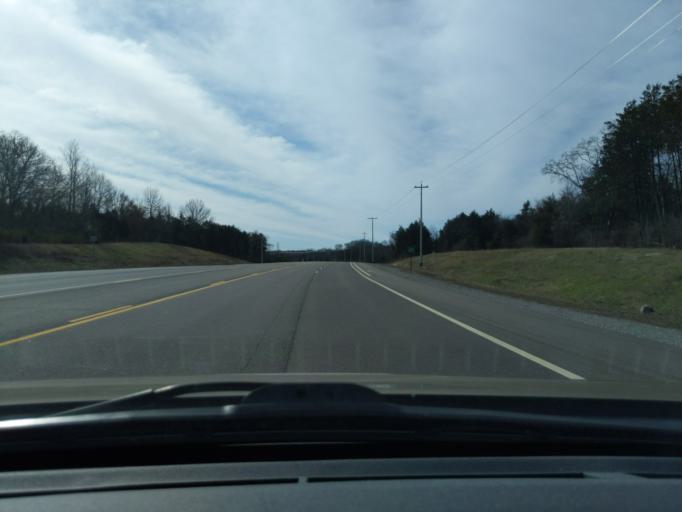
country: US
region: Tennessee
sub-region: Wilson County
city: Mount Juliet
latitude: 36.2088
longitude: -86.4969
